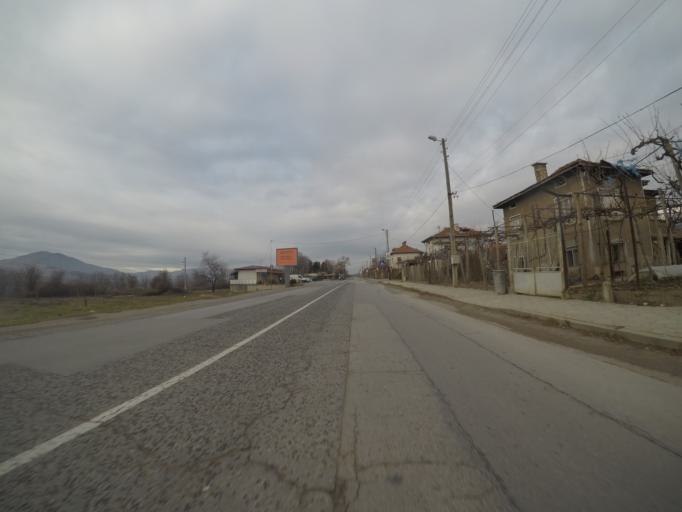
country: BG
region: Kyustendil
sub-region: Obshtina Kocherinovo
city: Kocherinovo
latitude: 42.1157
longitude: 23.0383
